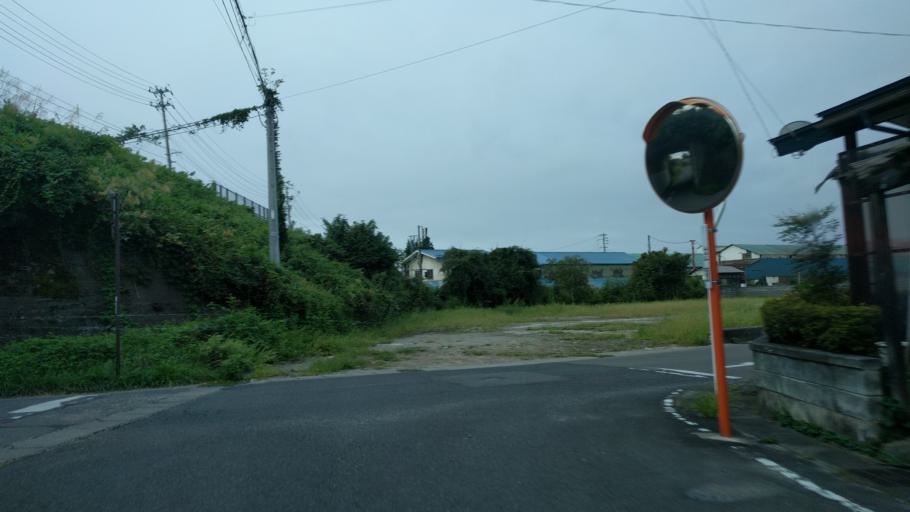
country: JP
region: Fukushima
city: Kitakata
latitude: 37.6452
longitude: 139.8612
